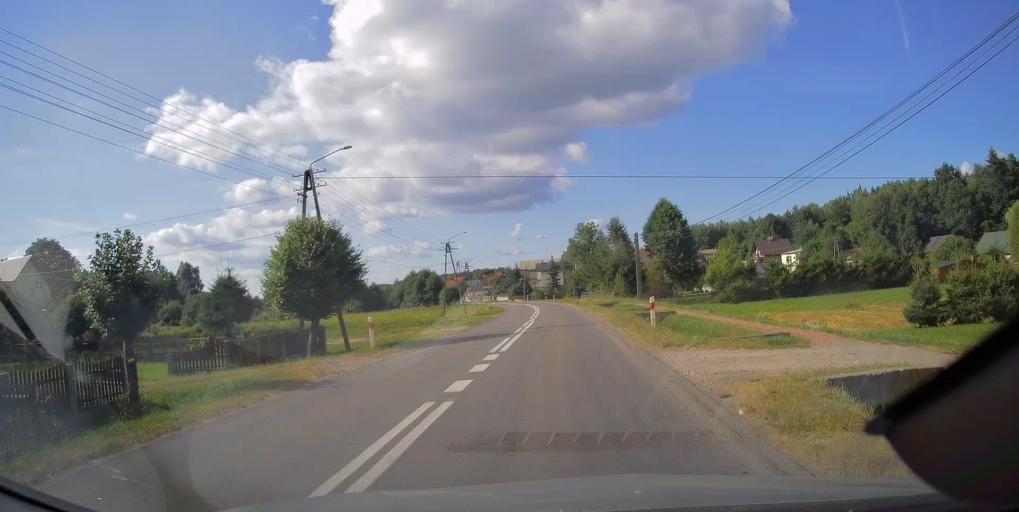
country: PL
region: Swietokrzyskie
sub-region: Powiat skarzyski
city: Suchedniow
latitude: 51.0014
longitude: 20.8502
